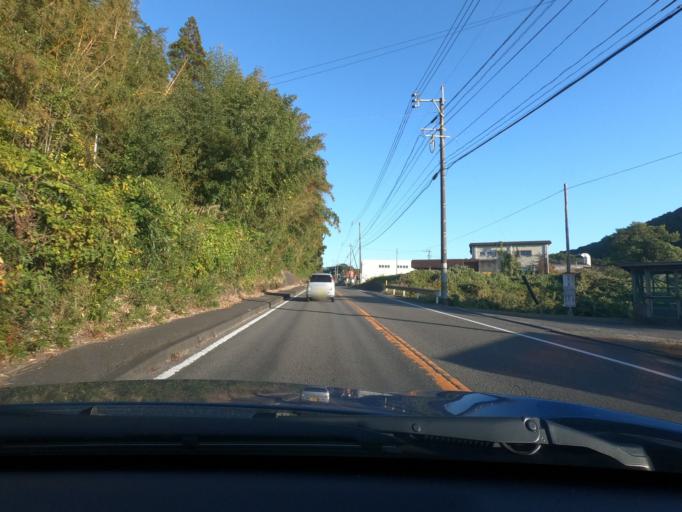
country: JP
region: Kagoshima
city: Satsumasendai
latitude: 31.8477
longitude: 130.2512
